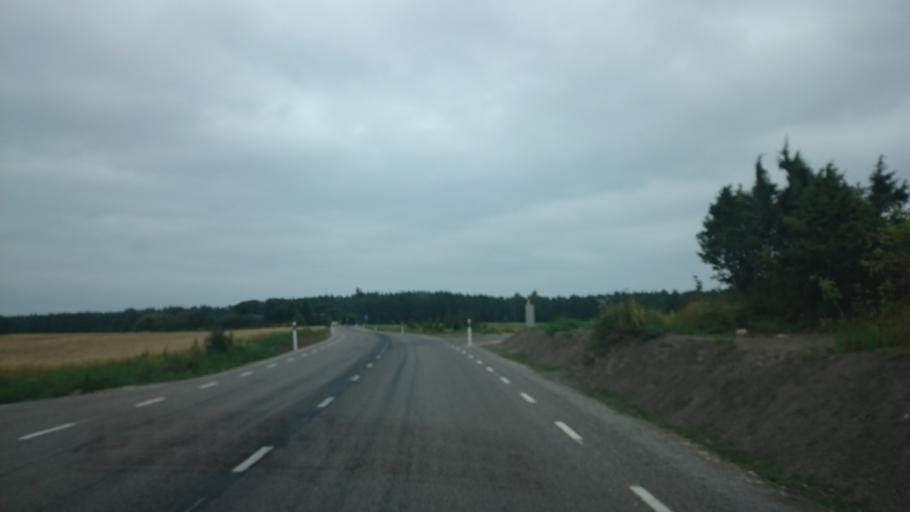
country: EE
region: Saare
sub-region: Orissaare vald
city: Orissaare
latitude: 58.5852
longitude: 22.7064
